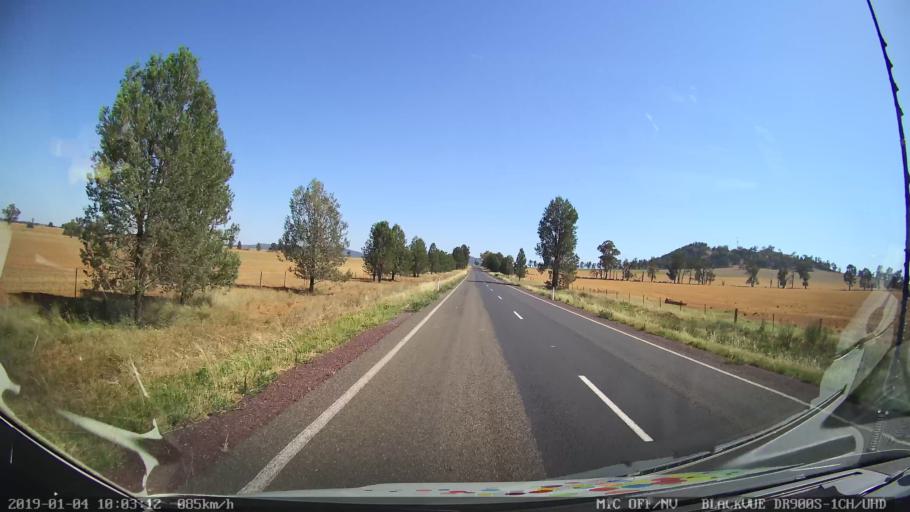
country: AU
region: New South Wales
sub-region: Cabonne
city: Canowindra
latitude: -33.4667
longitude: 148.3647
